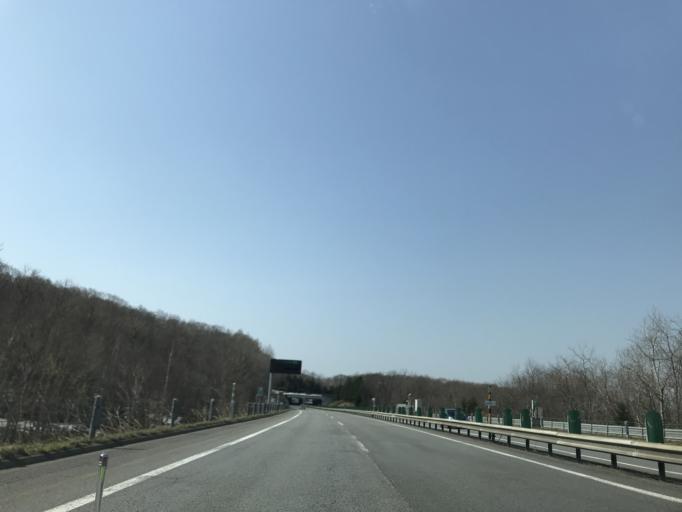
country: JP
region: Hokkaido
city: Bibai
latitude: 43.2929
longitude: 141.8663
